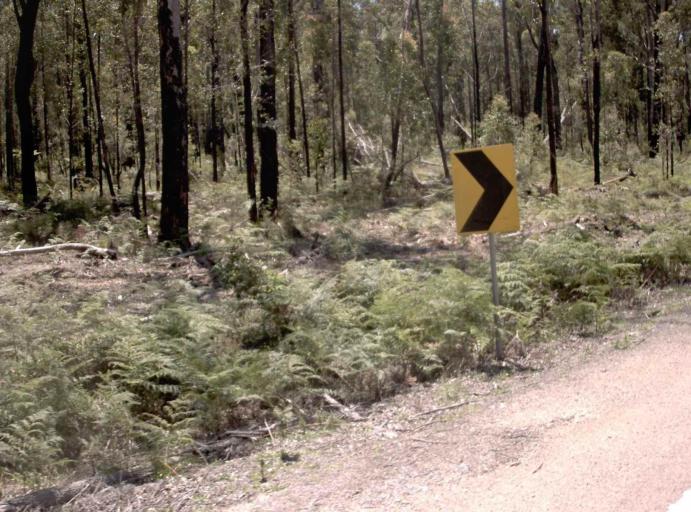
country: AU
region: Victoria
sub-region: East Gippsland
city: Lakes Entrance
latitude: -37.6887
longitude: 148.7503
